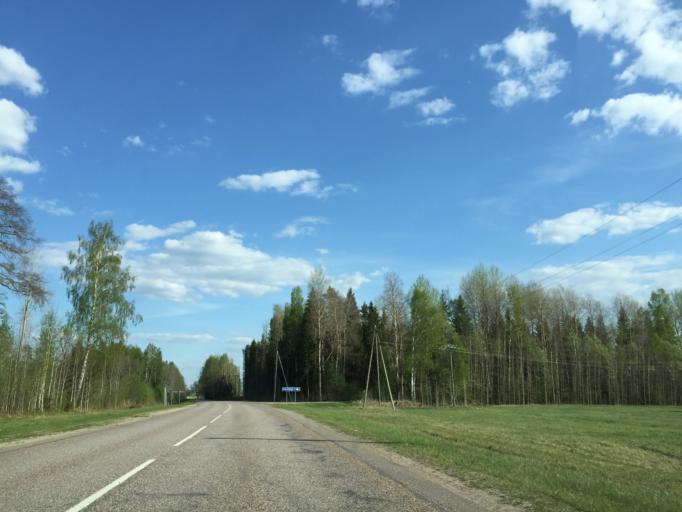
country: LV
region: Limbazu Rajons
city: Limbazi
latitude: 57.4936
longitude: 24.8471
